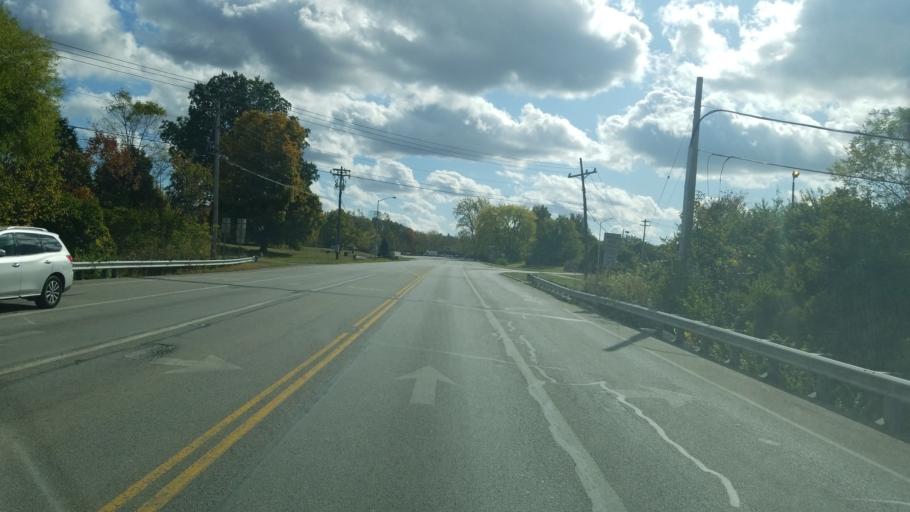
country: US
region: Ohio
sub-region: Warren County
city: Lebanon
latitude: 39.4315
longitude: -84.1888
